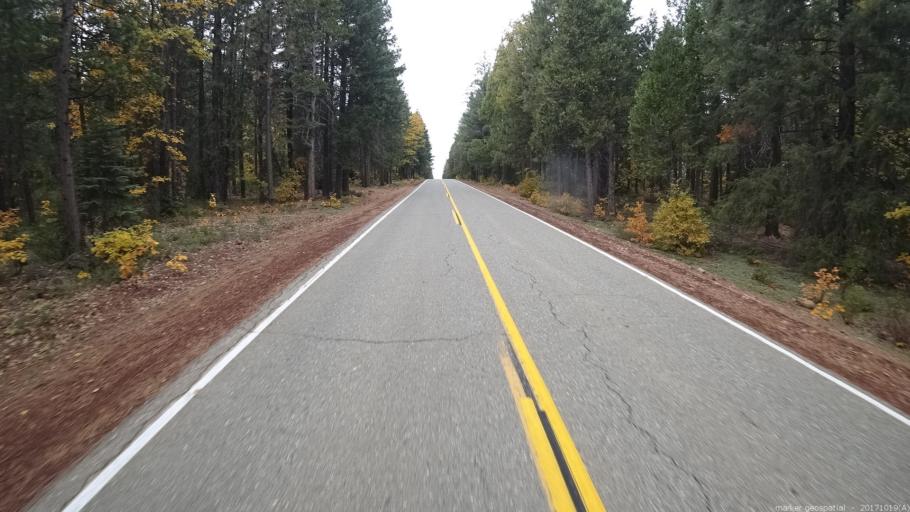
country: US
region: California
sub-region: Shasta County
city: Burney
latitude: 41.1385
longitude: -121.6223
